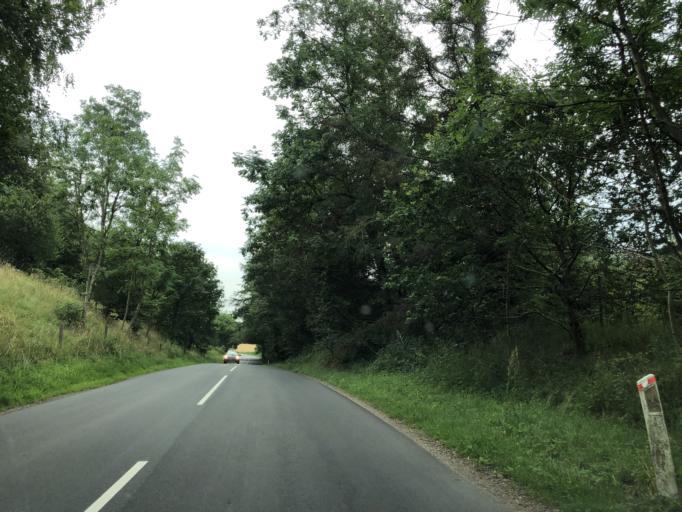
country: DK
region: Central Jutland
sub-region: Viborg Kommune
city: Stoholm
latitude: 56.4535
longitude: 9.1666
